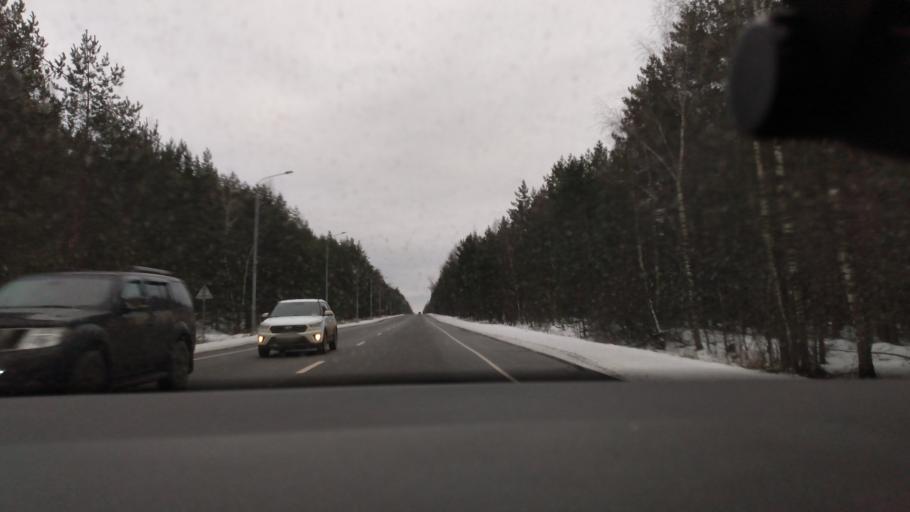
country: RU
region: Moskovskaya
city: Il'inskiy Pogost
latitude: 55.4705
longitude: 38.9624
